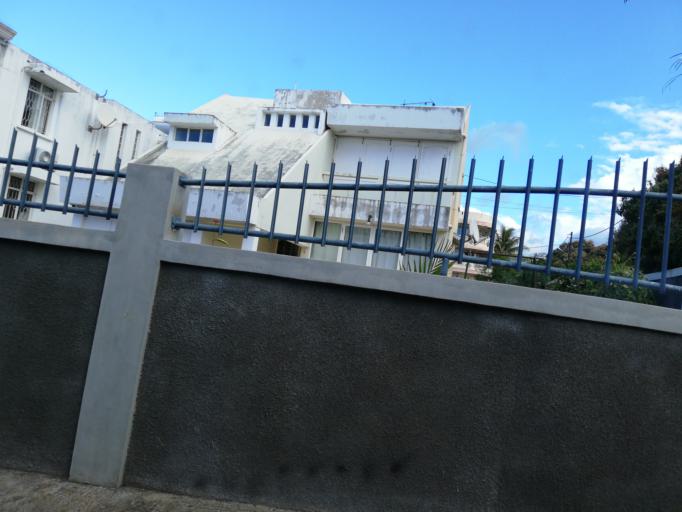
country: MU
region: Moka
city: Pailles
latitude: -20.1979
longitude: 57.4678
